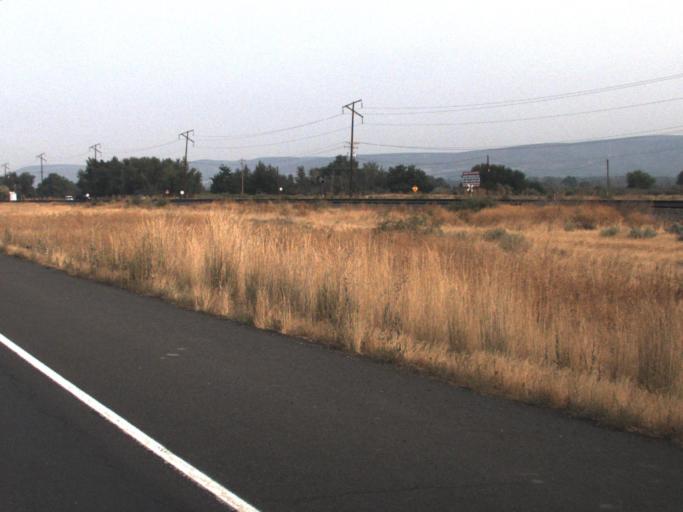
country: US
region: Washington
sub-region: Yakima County
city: Wapato
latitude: 46.4597
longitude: -120.4328
